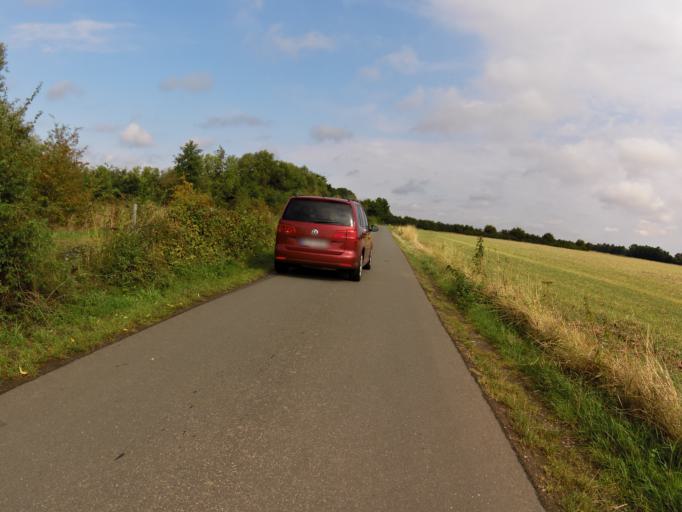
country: DE
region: Lower Saxony
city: Marklohe
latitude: 52.6912
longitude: 9.1787
